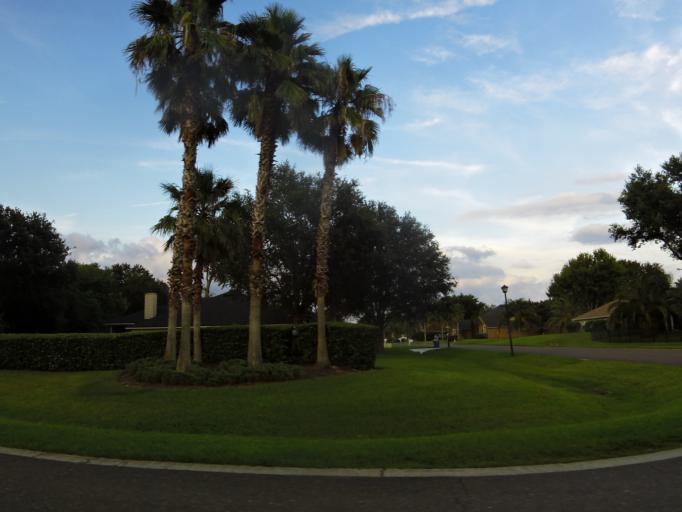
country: US
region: Florida
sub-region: Duval County
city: Atlantic Beach
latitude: 30.3973
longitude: -81.4975
